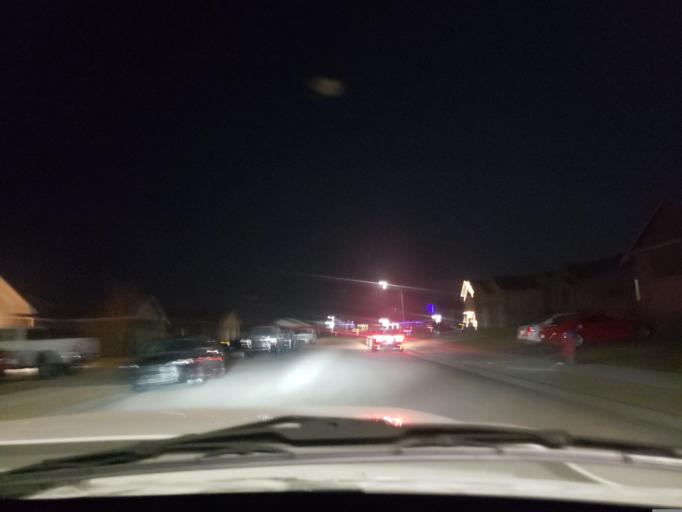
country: US
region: Kansas
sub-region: Finney County
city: Garden City
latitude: 37.9856
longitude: -100.8256
